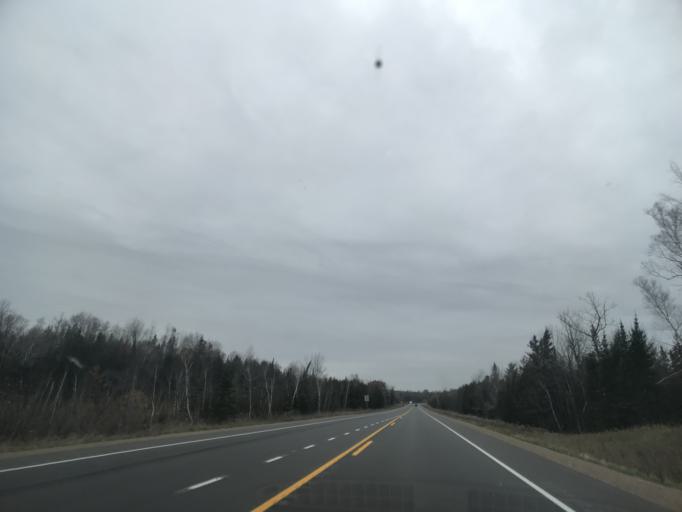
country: US
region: Wisconsin
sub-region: Menominee County
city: Legend Lake
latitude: 45.2579
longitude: -88.5138
